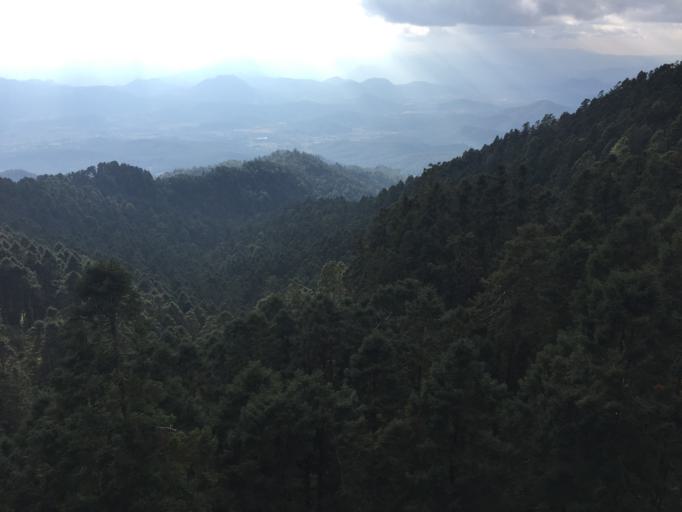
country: MX
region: Michoacan
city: Mineral de Angangueo
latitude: 19.6709
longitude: -100.2896
